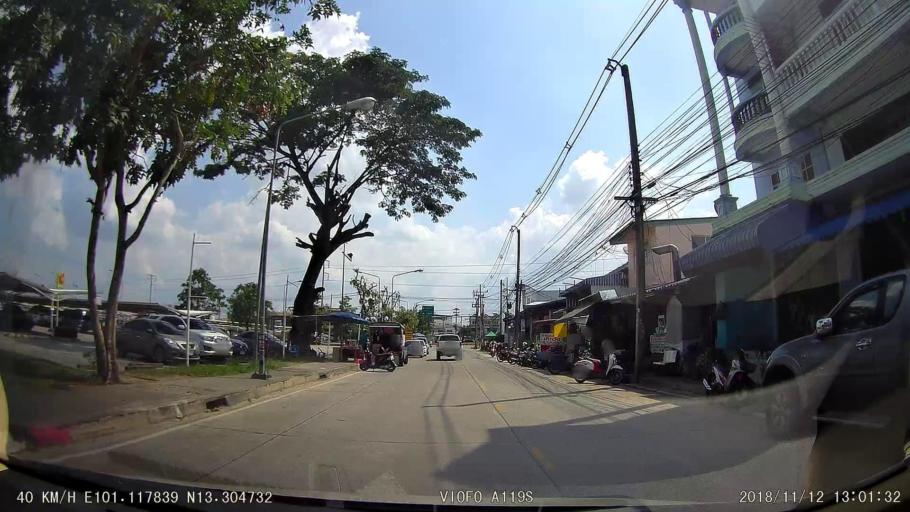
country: TH
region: Chon Buri
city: Ban Bueng
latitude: 13.3046
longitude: 101.1179
